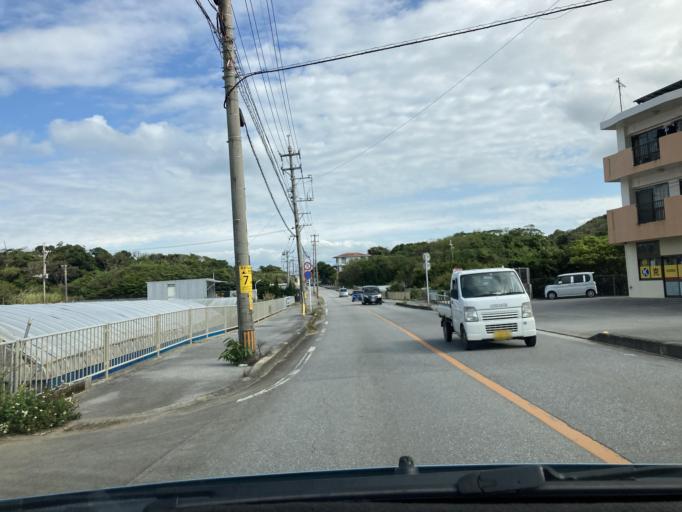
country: JP
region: Okinawa
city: Nago
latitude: 26.6934
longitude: 127.9552
